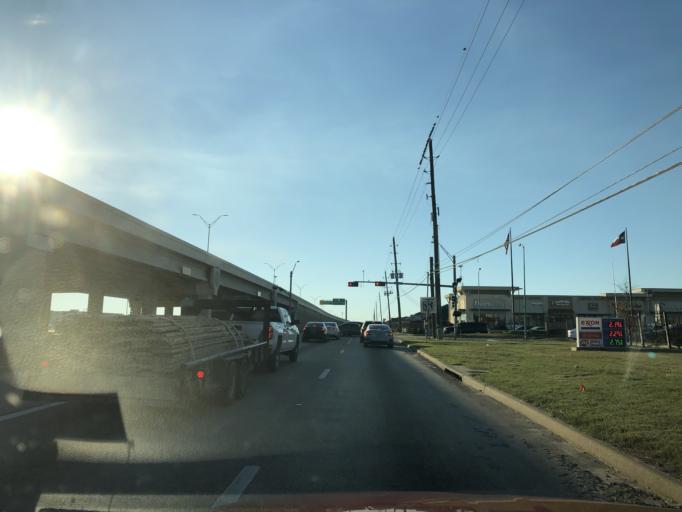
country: US
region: Texas
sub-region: Fort Bend County
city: Cinco Ranch
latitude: 29.7018
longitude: -95.7595
